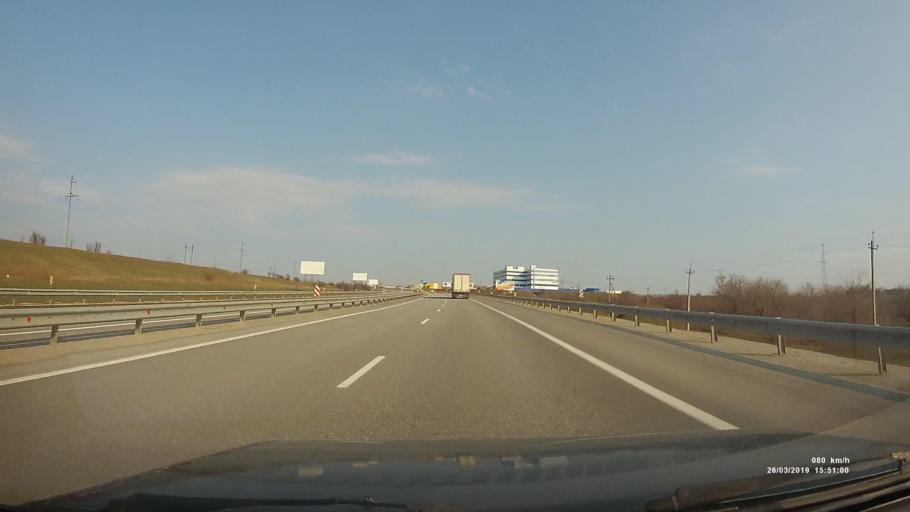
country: RU
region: Rostov
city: Chaltyr
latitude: 47.2706
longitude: 39.4967
